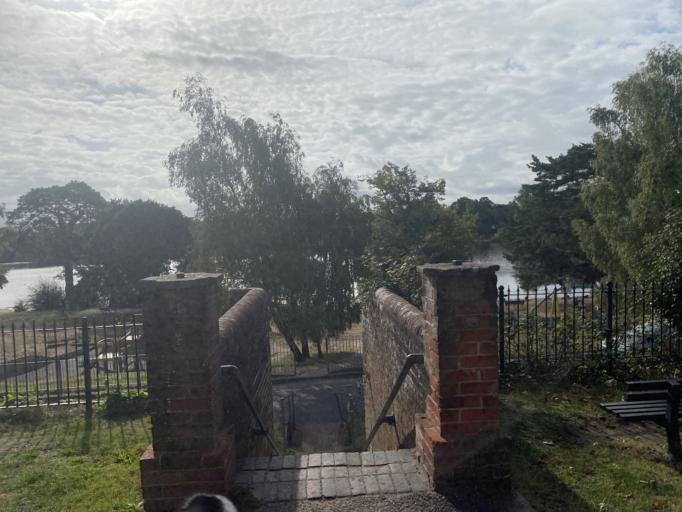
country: GB
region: England
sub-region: Hampshire
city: Petersfield
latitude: 51.0013
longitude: -0.9310
